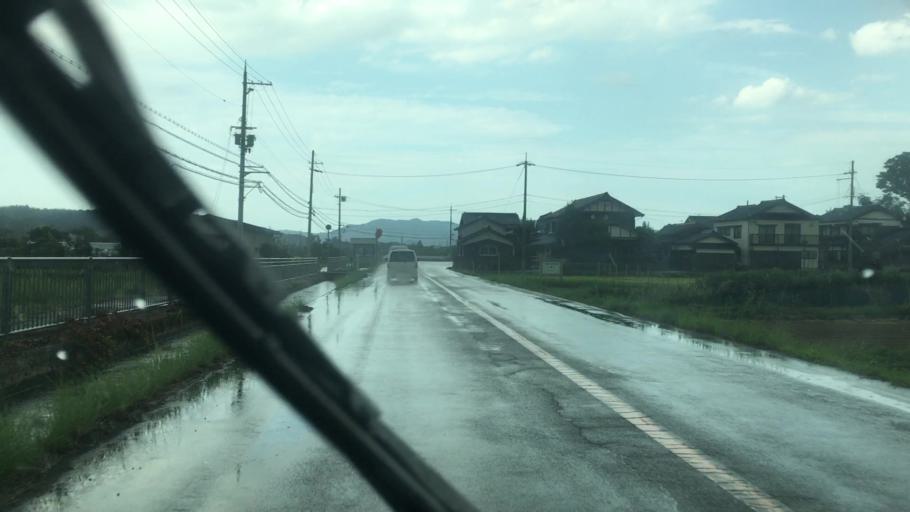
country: JP
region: Hyogo
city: Toyooka
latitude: 35.4960
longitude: 134.8163
